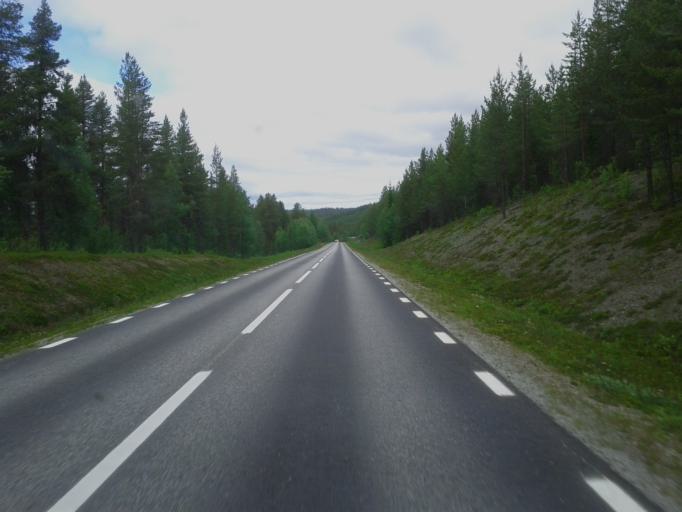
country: SE
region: Vaesterbotten
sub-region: Storumans Kommun
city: Fristad
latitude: 65.3736
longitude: 16.5166
